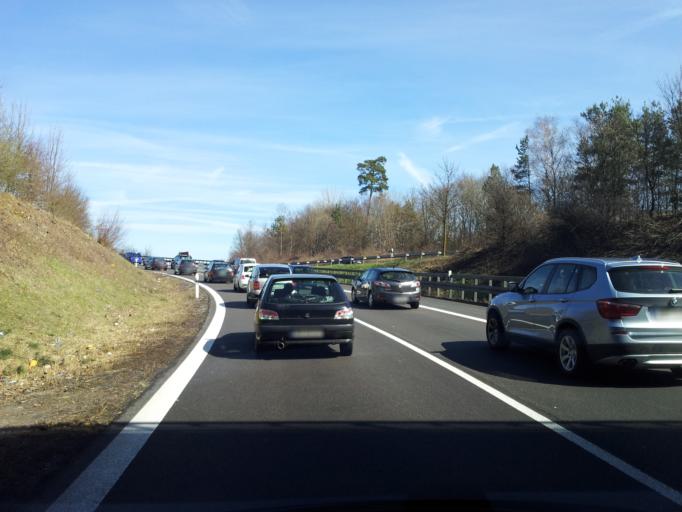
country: DE
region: Baden-Wuerttemberg
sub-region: Regierungsbezirk Stuttgart
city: Sindelfingen
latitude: 48.7255
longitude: 9.0706
